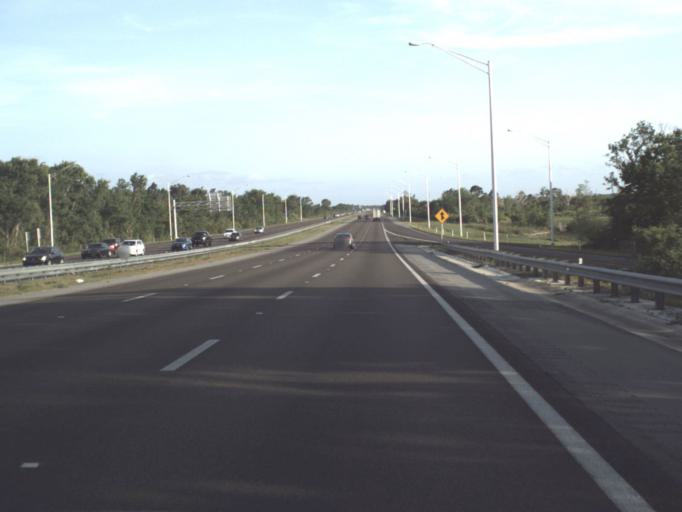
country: US
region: Florida
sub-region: Volusia County
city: Oak Hill
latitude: 28.7693
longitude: -80.8935
